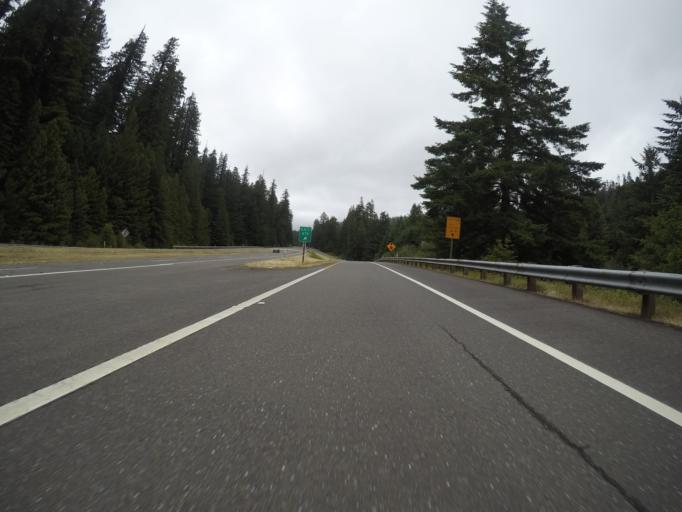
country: US
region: California
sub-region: Humboldt County
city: Rio Dell
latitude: 40.4397
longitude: -124.0344
